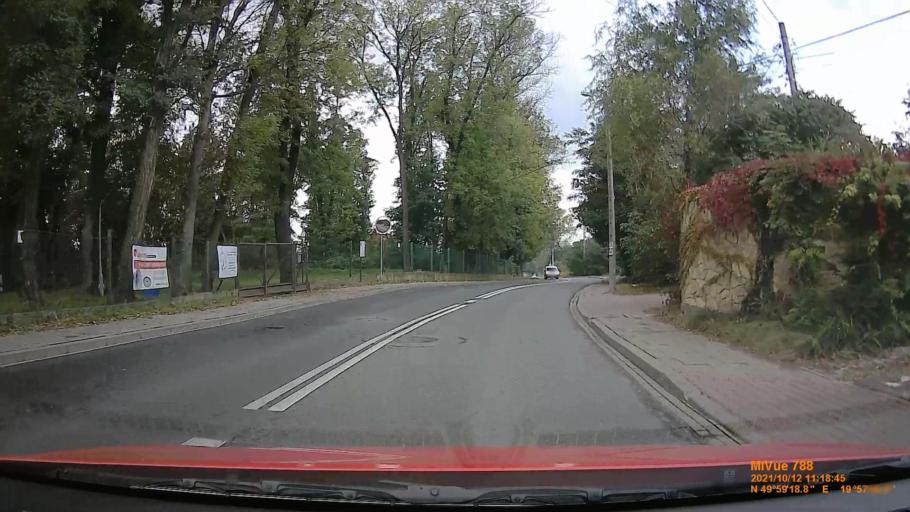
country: PL
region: Lesser Poland Voivodeship
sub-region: Powiat krakowski
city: Wrzasowice
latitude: 49.9886
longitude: 19.9592
